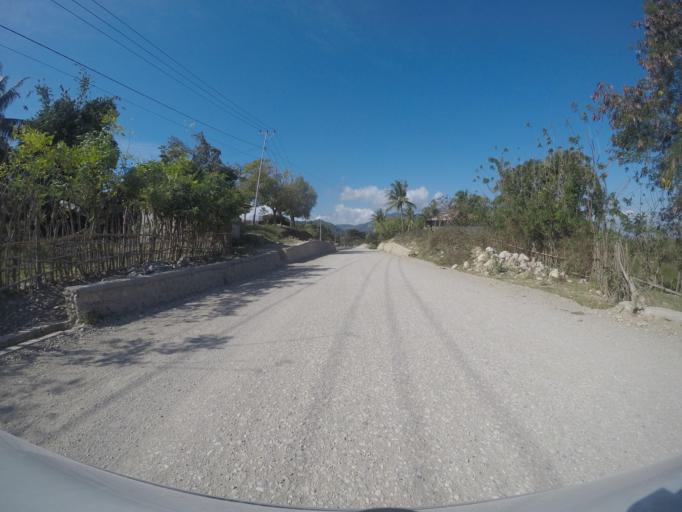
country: TL
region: Viqueque
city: Viqueque
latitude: -8.8162
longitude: 126.5343
